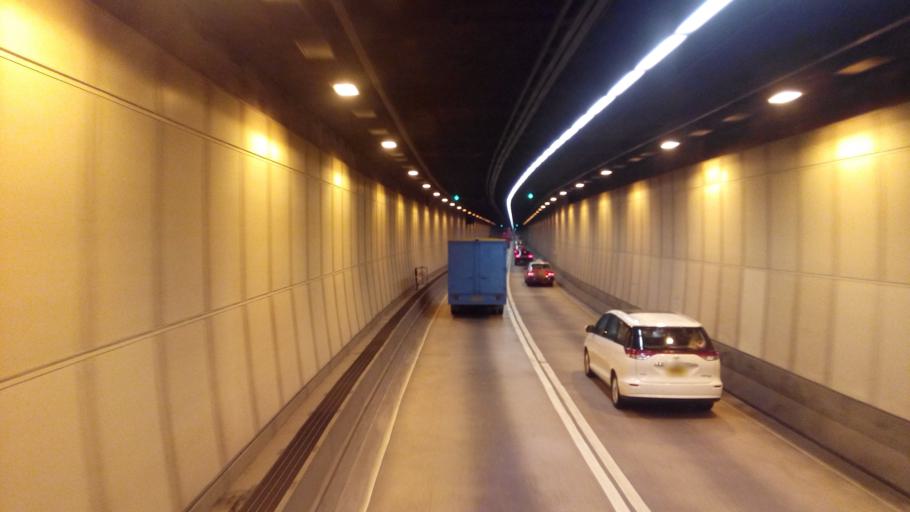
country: HK
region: Wanchai
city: Wan Chai
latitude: 22.2699
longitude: 114.1809
